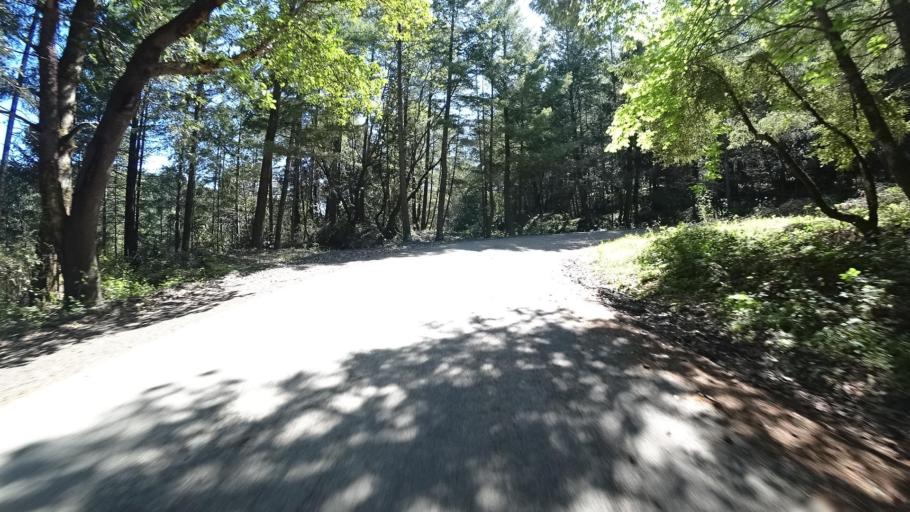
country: US
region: California
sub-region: Humboldt County
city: Rio Dell
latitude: 40.2184
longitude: -124.1085
